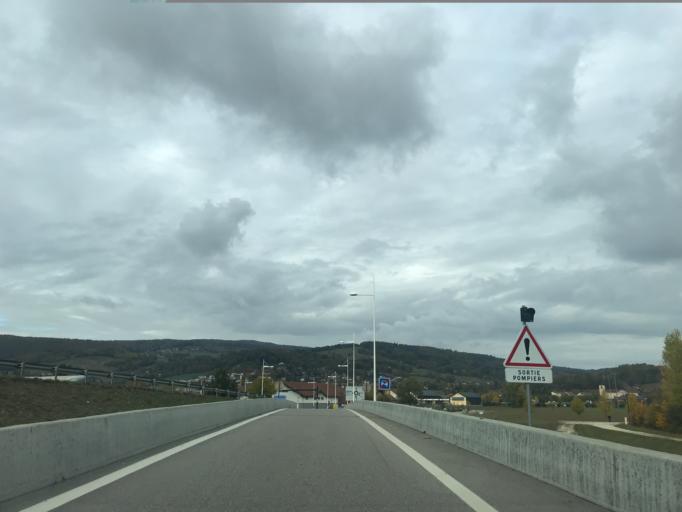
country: FR
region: Rhone-Alpes
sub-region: Departement de la Haute-Savoie
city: Epagny
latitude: 45.9315
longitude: 6.0855
